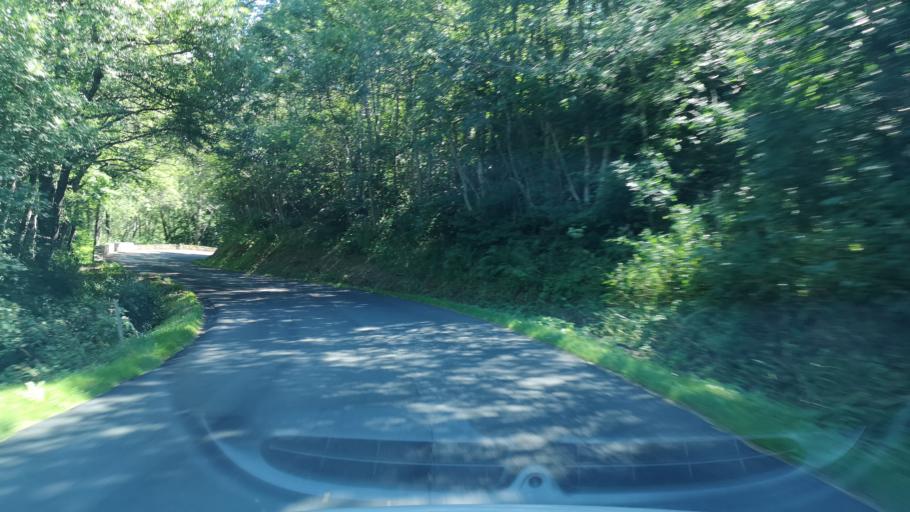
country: FR
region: Auvergne
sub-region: Departement du Puy-de-Dome
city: Mont-Dore
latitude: 45.5772
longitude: 2.8828
